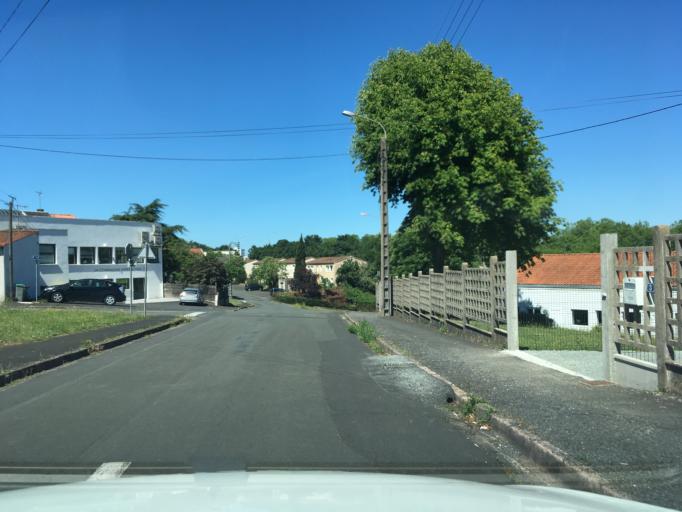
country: FR
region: Poitou-Charentes
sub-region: Departement des Deux-Sevres
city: Niort
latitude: 46.3226
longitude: -0.4472
